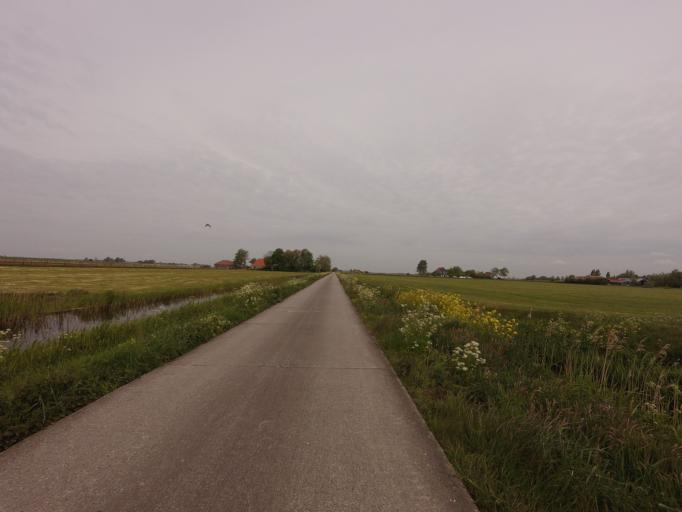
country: NL
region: Friesland
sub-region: Sudwest Fryslan
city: Workum
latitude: 53.0224
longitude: 5.4590
